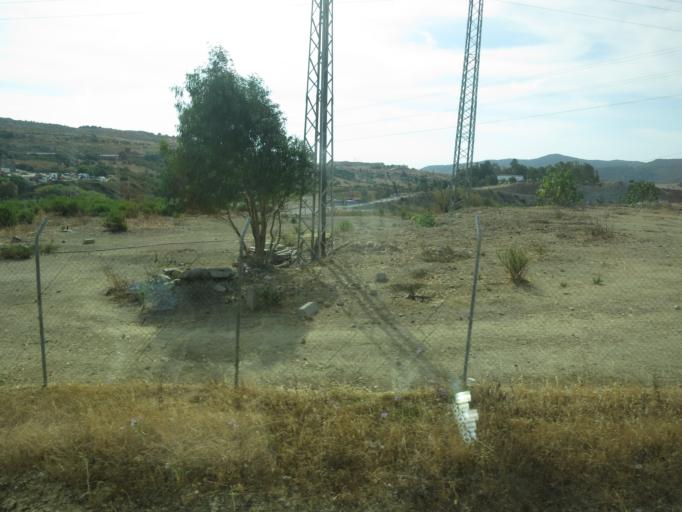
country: ES
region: Andalusia
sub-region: Provincia de Cadiz
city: Algeciras
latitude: 36.1072
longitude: -5.4598
